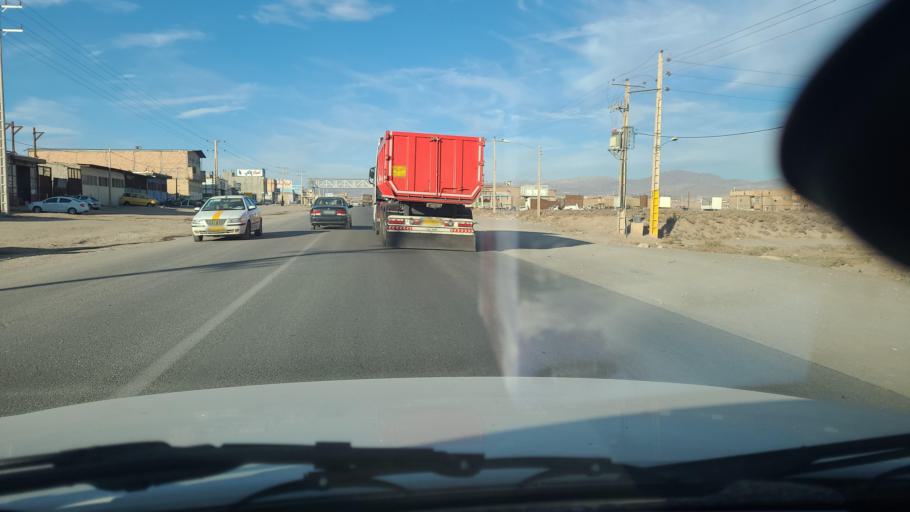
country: IR
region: Razavi Khorasan
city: Sabzevar
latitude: 36.2196
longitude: 57.6514
